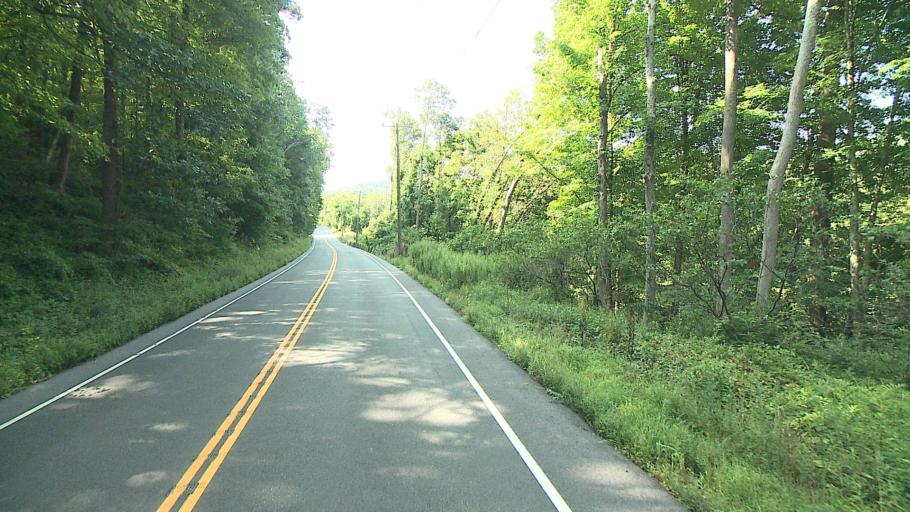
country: US
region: Connecticut
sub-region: Litchfield County
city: Kent
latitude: 41.6563
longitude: -73.4897
